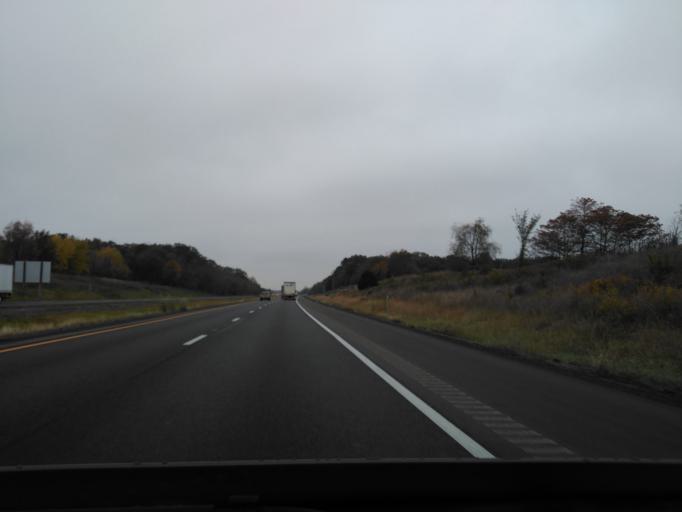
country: US
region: Illinois
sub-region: Madison County
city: Highland
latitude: 38.7866
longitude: -89.6595
